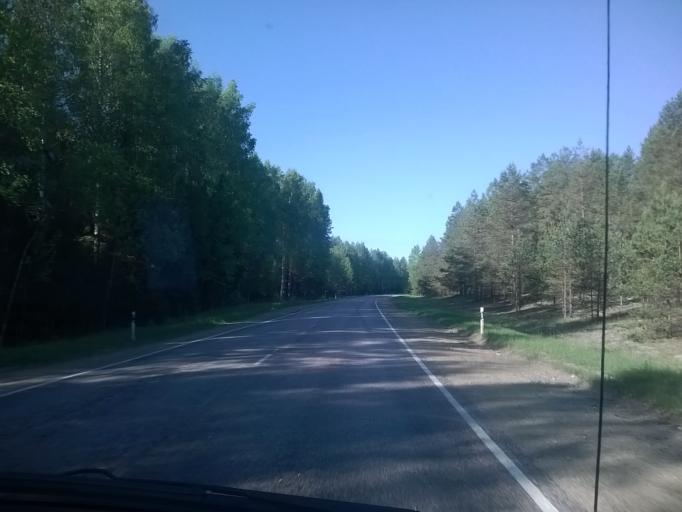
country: LV
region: Strenci
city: Seda
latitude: 57.6381
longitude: 25.8315
